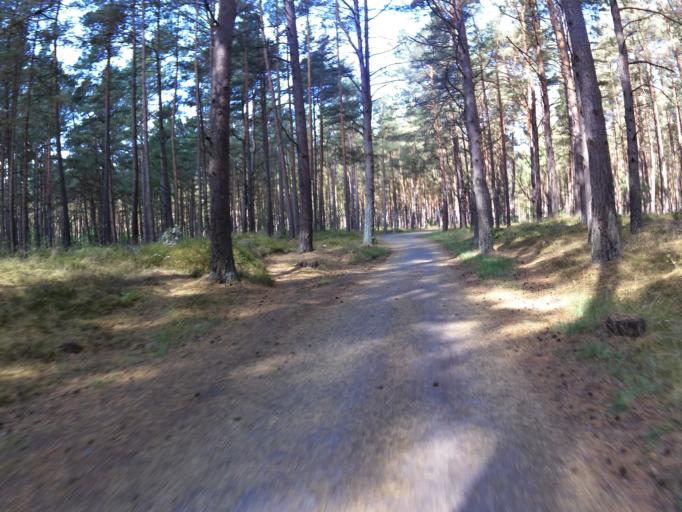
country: DE
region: Mecklenburg-Vorpommern
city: Karlshagen
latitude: 54.1023
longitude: 13.8577
